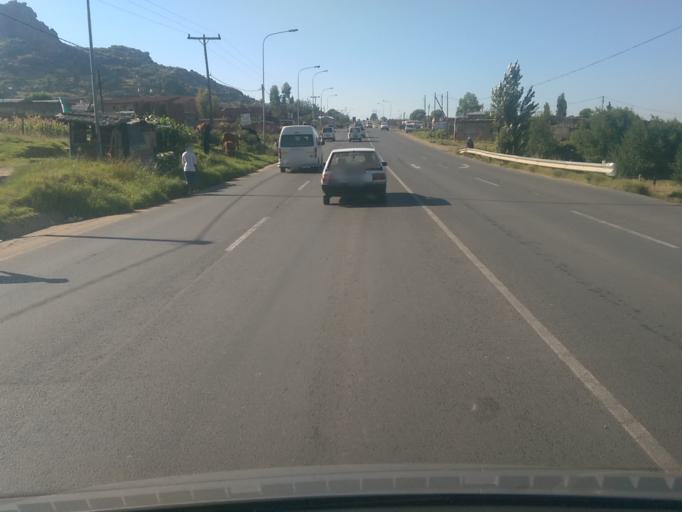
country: LS
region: Maseru
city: Maseru
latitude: -29.3484
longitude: 27.5188
